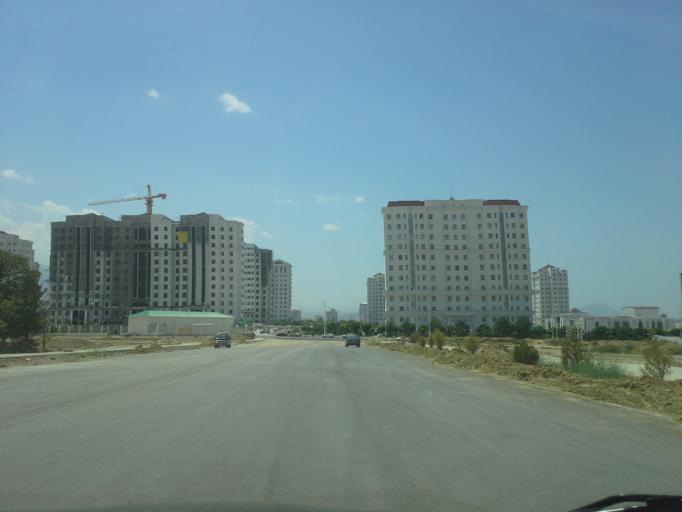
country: TM
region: Ahal
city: Ashgabat
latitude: 37.8903
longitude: 58.3984
